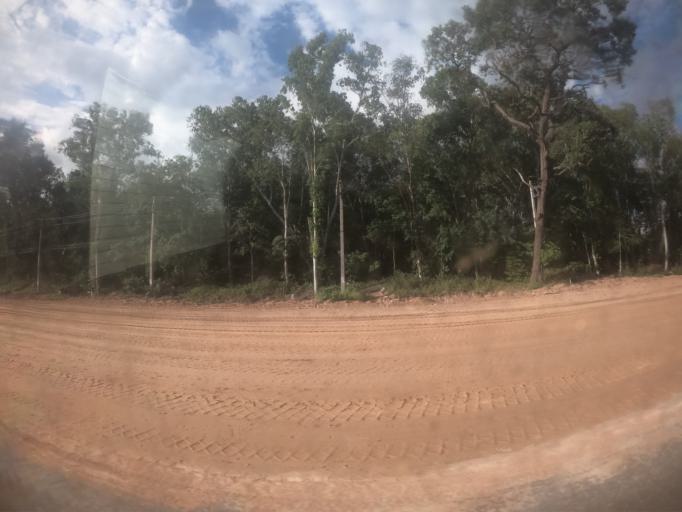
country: TH
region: Surin
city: Kap Choeng
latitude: 14.4774
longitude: 103.5887
